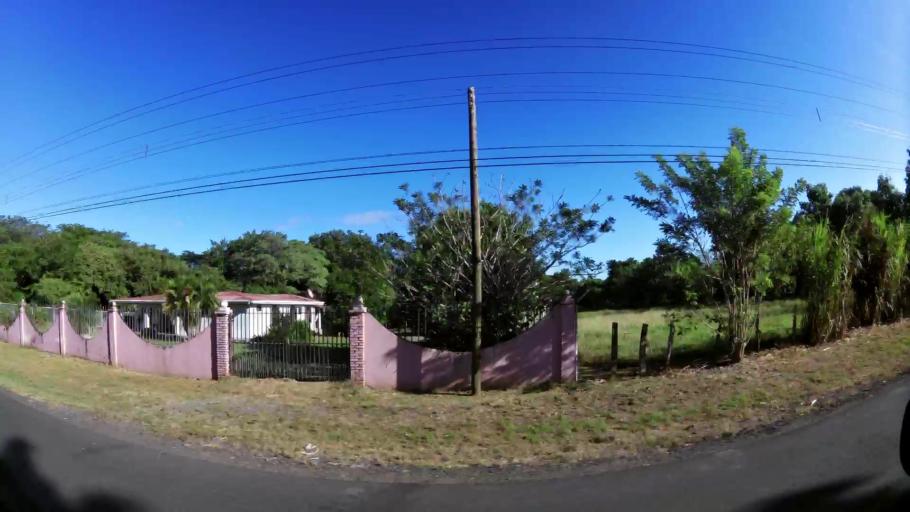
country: CR
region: Guanacaste
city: Sardinal
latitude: 10.4902
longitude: -85.6282
